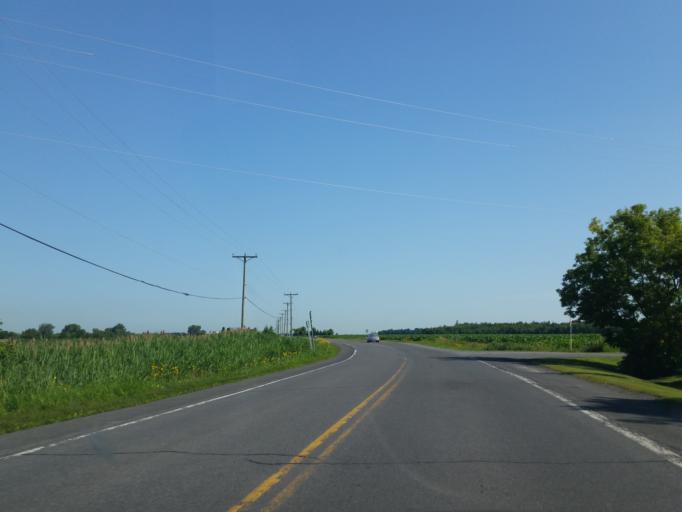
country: CA
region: Quebec
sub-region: Monteregie
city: Napierville
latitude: 45.2146
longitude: -73.3937
